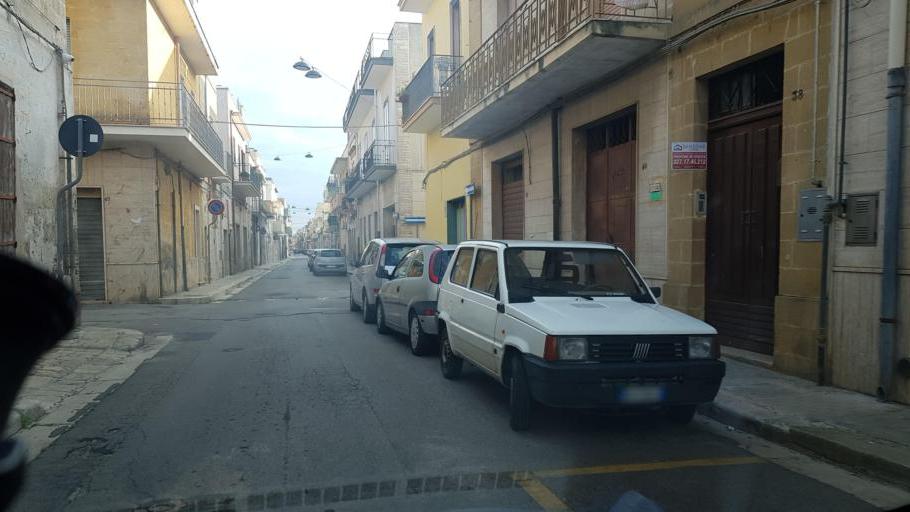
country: IT
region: Apulia
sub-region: Provincia di Brindisi
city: Francavilla Fontana
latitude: 40.5302
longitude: 17.5788
